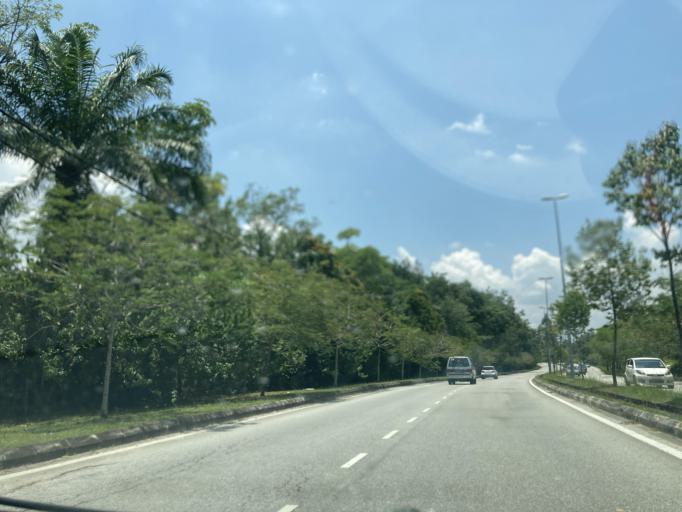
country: MY
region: Selangor
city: Batu Arang
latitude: 3.2954
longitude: 101.4858
